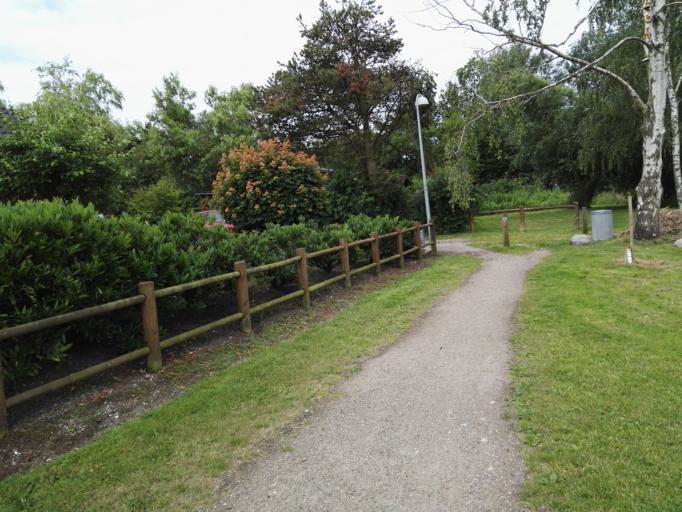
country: DK
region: Zealand
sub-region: Roskilde Kommune
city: Jyllinge
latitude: 55.7774
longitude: 12.0970
